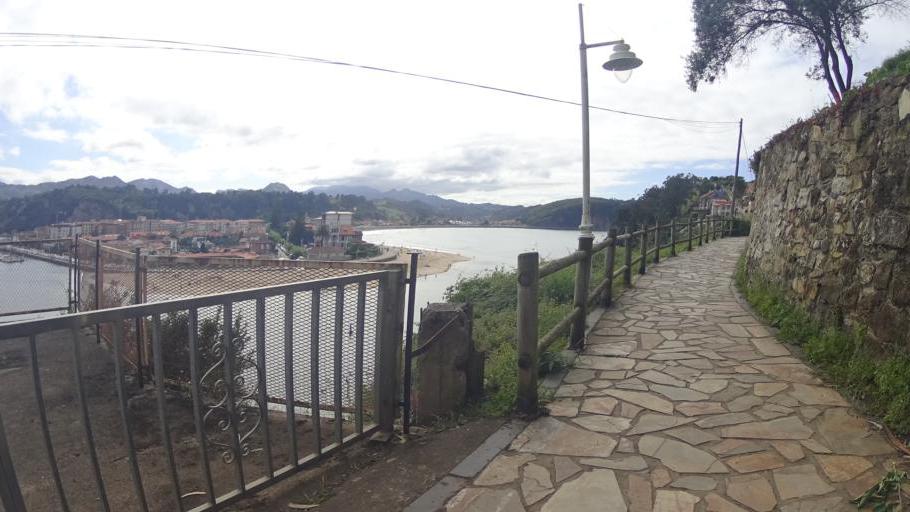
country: ES
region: Asturias
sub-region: Province of Asturias
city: Ribadesella
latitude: 43.4669
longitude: -5.0601
